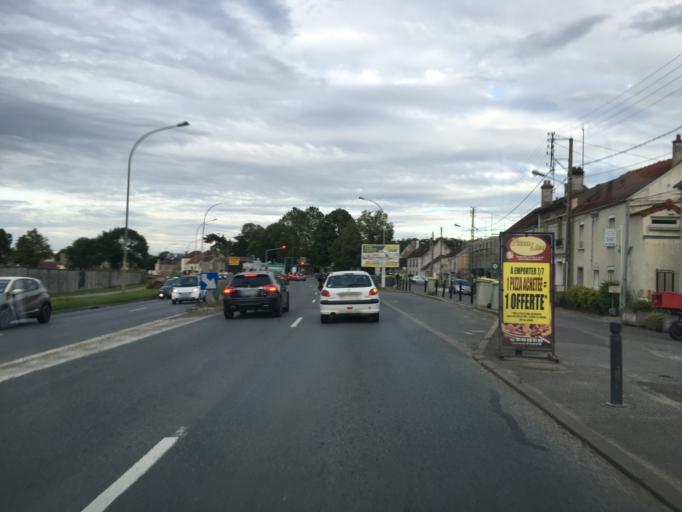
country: FR
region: Ile-de-France
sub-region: Departement du Val-de-Marne
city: Villecresnes
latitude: 48.7282
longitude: 2.5293
